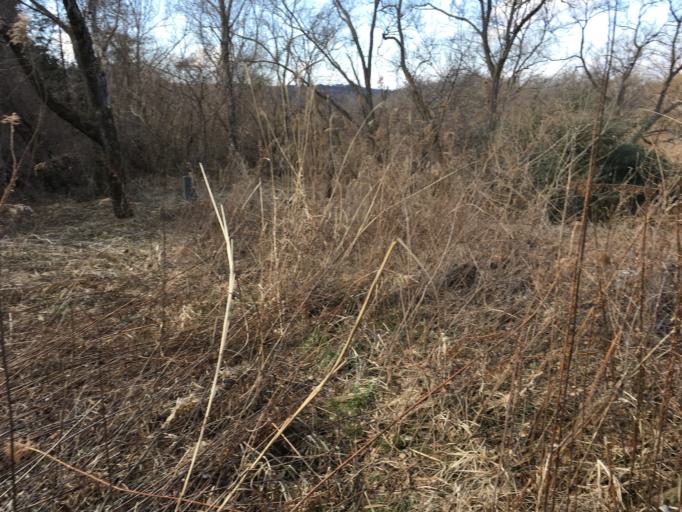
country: JP
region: Iwate
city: Ichinoseki
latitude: 38.8329
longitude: 141.2651
